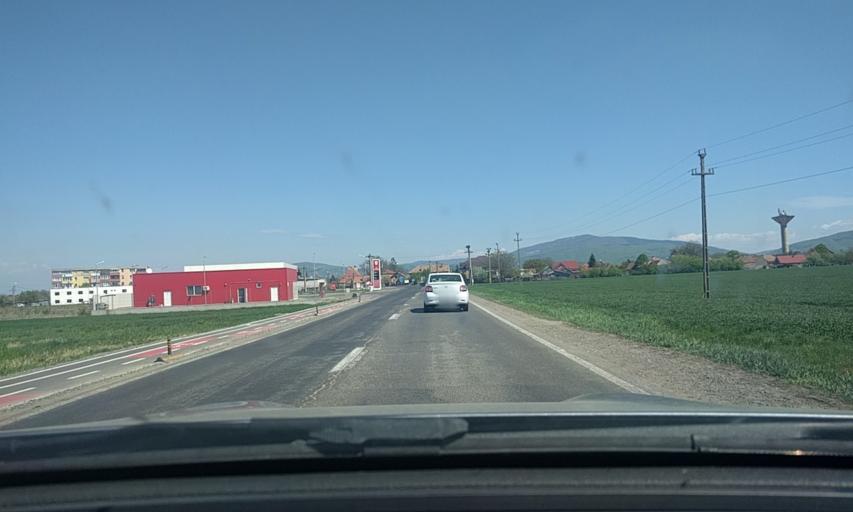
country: RO
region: Brasov
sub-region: Comuna Prejmer
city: Prejmer
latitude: 45.7173
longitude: 25.7606
